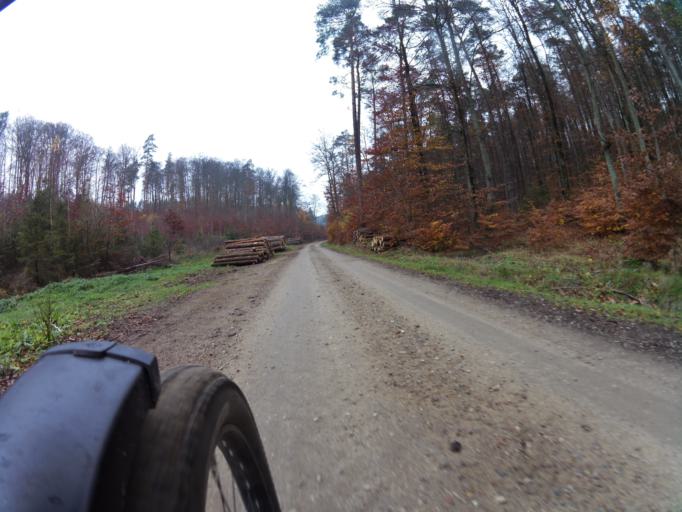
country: PL
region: Pomeranian Voivodeship
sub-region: Powiat wejherowski
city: Orle
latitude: 54.7039
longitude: 18.1456
